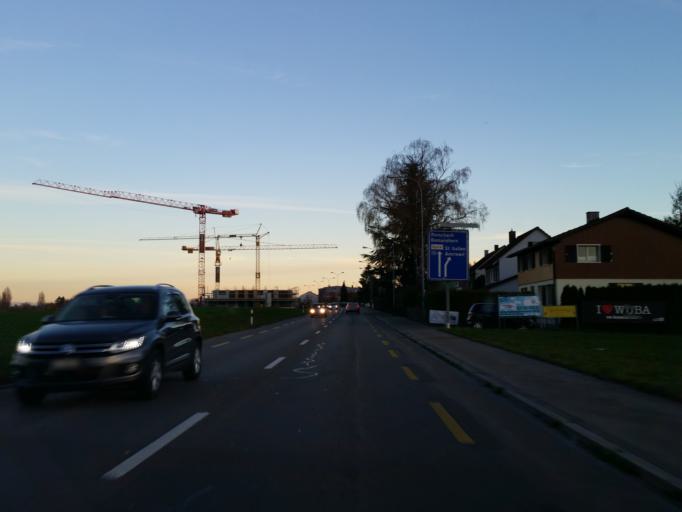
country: CH
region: Thurgau
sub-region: Kreuzlingen District
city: Bottighofen
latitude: 47.6364
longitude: 9.2170
